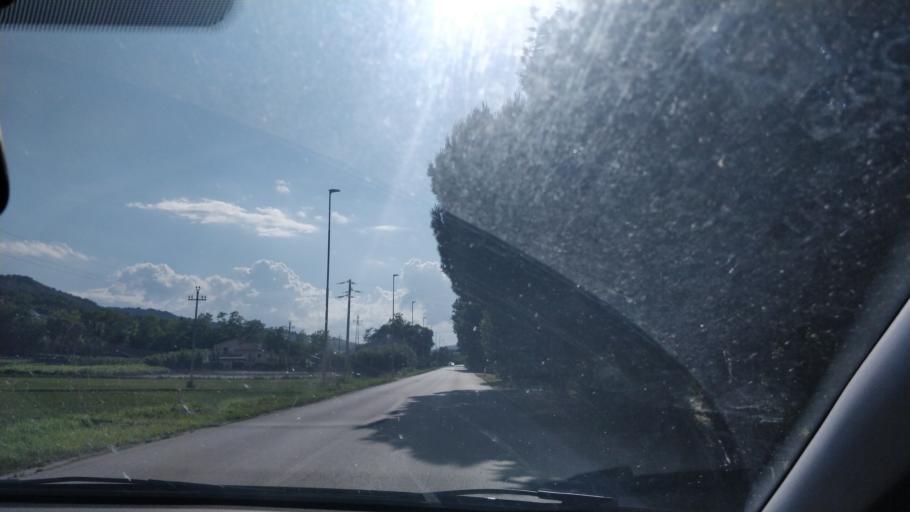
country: IT
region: The Marches
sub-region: Provincia di Ascoli Piceno
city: Massignano
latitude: 43.0363
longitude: 13.8243
